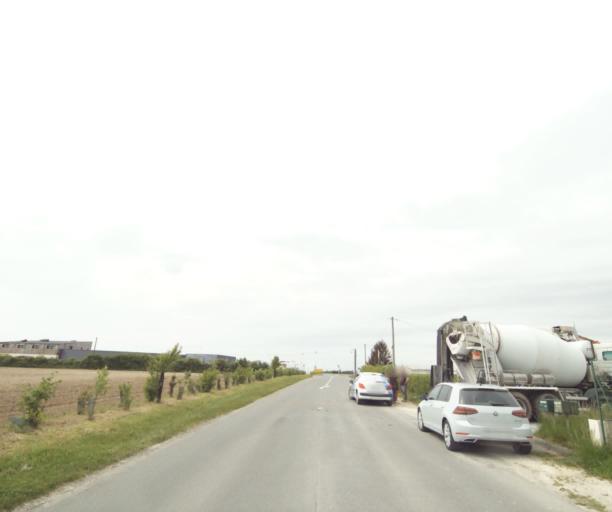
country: FR
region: Poitou-Charentes
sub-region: Departement de la Charente-Maritime
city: Les Gonds
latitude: 45.7068
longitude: -0.6251
